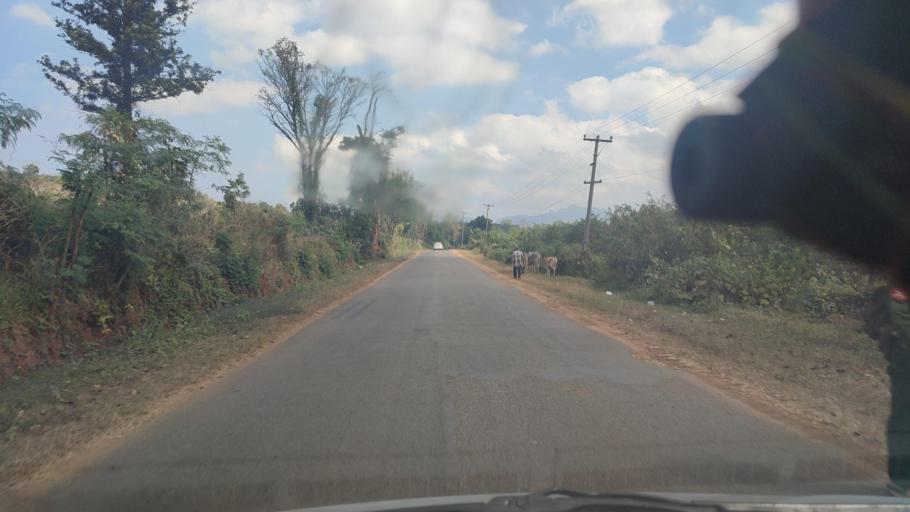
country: MM
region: Shan
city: Taunggyi
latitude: 21.3469
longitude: 96.8712
